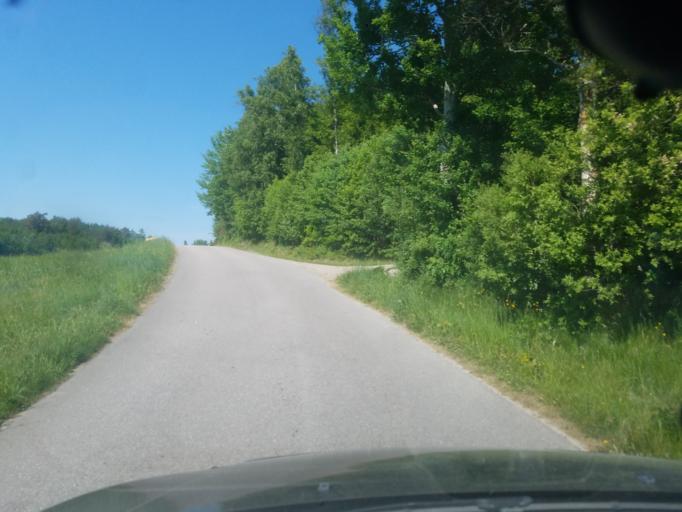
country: SE
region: Vaestra Goetaland
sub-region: Orust
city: Henan
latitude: 58.2766
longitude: 11.5772
